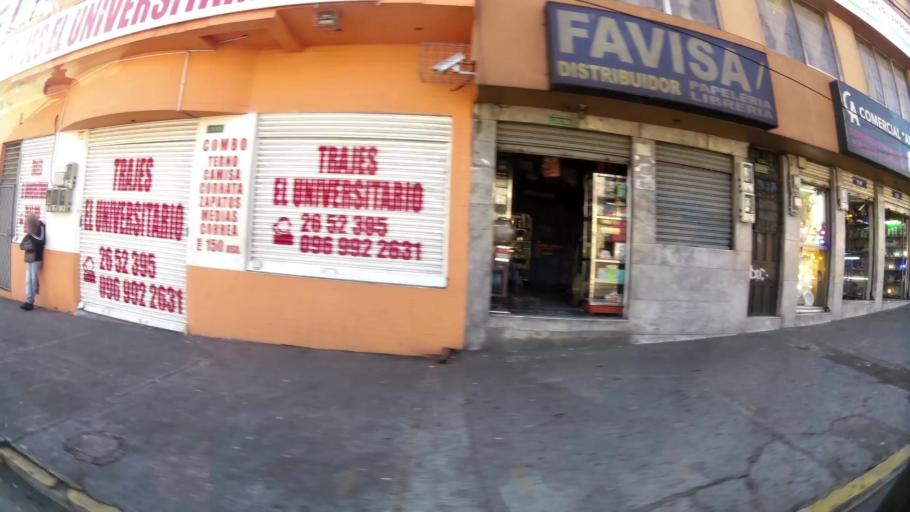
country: EC
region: Pichincha
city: Quito
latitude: -0.2466
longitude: -78.5344
